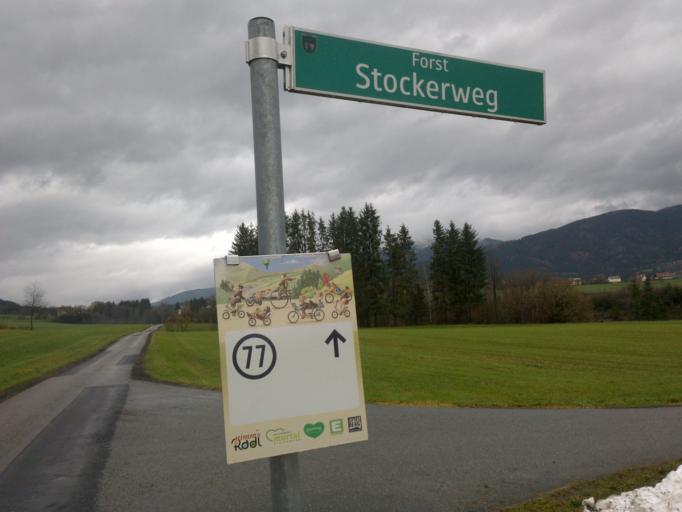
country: AT
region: Styria
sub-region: Politischer Bezirk Murtal
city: Seckau
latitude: 47.2598
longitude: 14.8070
